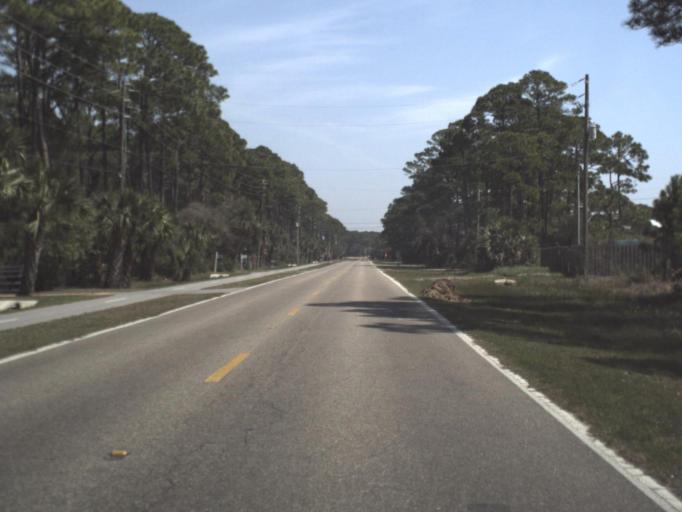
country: US
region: Florida
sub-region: Gulf County
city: Port Saint Joe
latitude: 29.6843
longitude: -85.3198
